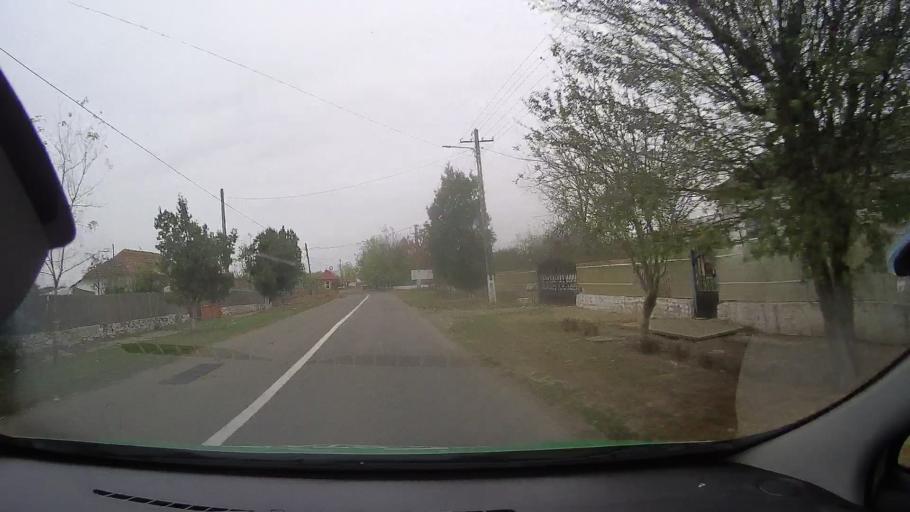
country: RO
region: Constanta
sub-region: Comuna Vulturu
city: Vulturu
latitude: 44.7057
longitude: 28.2342
